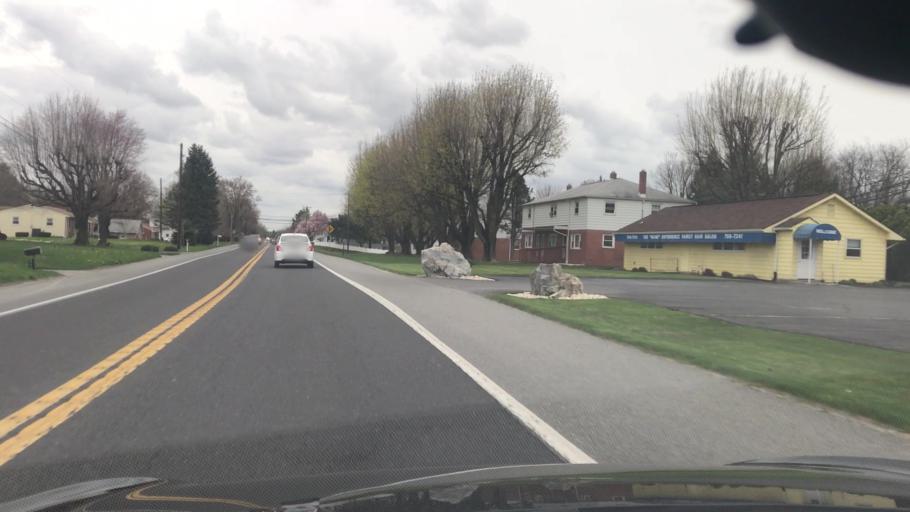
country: US
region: Pennsylvania
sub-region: Cumberland County
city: Mechanicsburg
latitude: 40.2287
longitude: -77.0310
